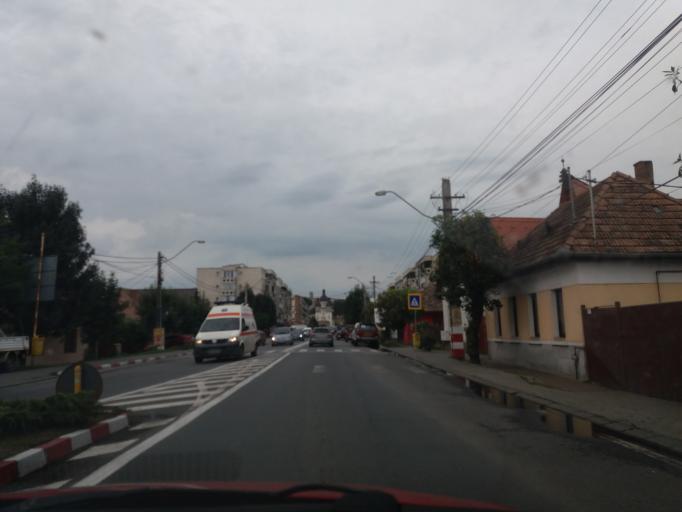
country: RO
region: Mures
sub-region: Municipiul Reghin
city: Reghin
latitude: 46.7714
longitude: 24.7032
